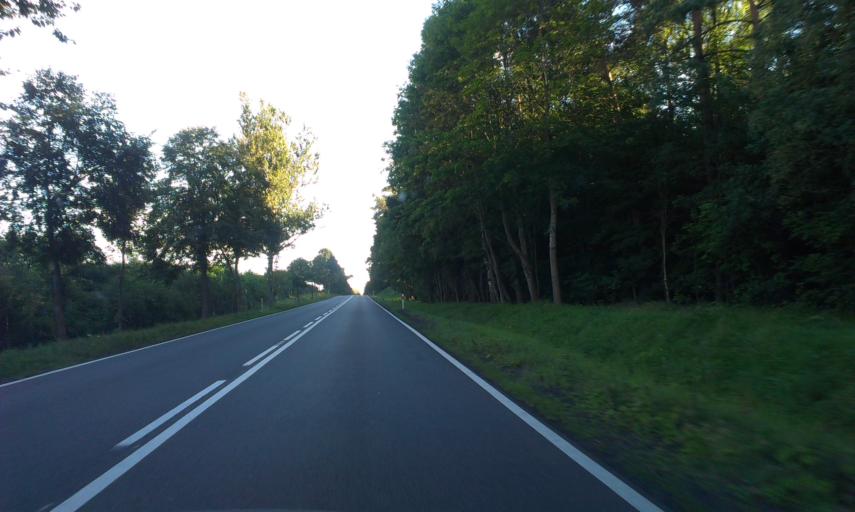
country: PL
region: West Pomeranian Voivodeship
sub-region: Powiat koszalinski
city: Bobolice
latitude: 53.8345
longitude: 16.6328
